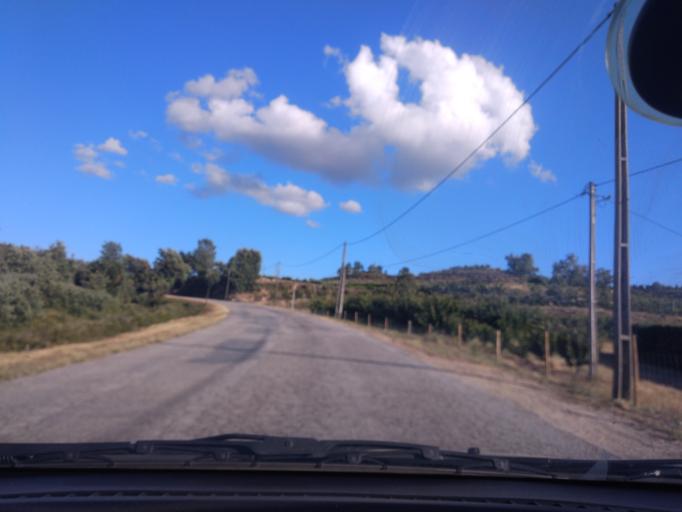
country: PT
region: Castelo Branco
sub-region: Covilha
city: Teixoso
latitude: 40.2375
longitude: -7.3854
